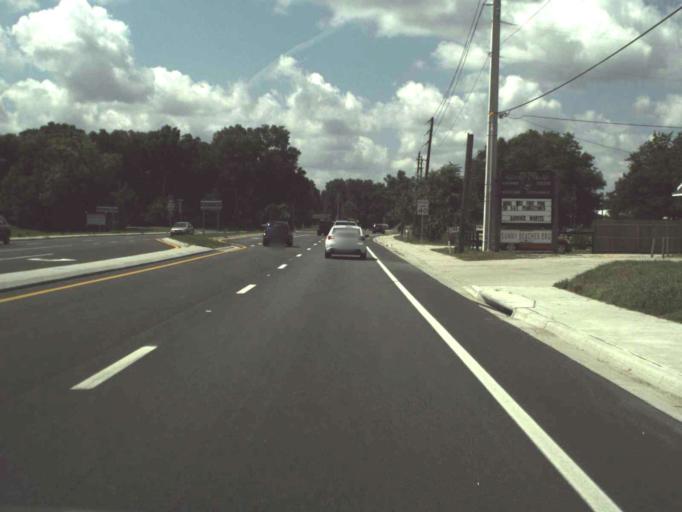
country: US
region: Florida
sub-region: Seminole County
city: Midway
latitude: 28.8495
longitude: -81.1622
